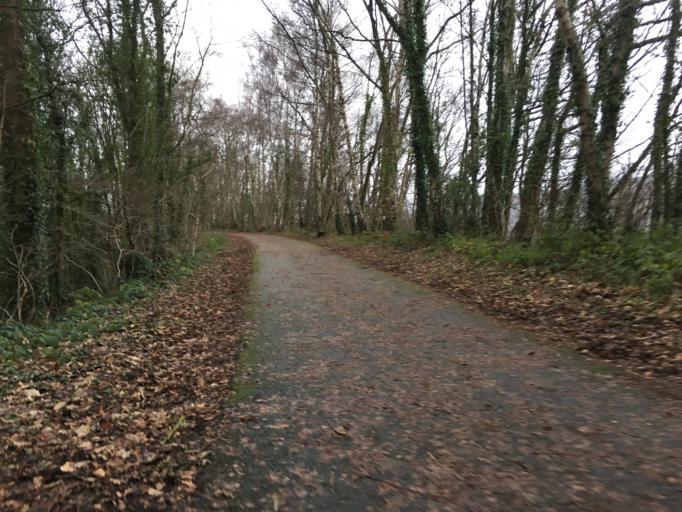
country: GB
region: Wales
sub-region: Monmouthshire
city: Abergavenny
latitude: 51.8183
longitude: -3.0435
